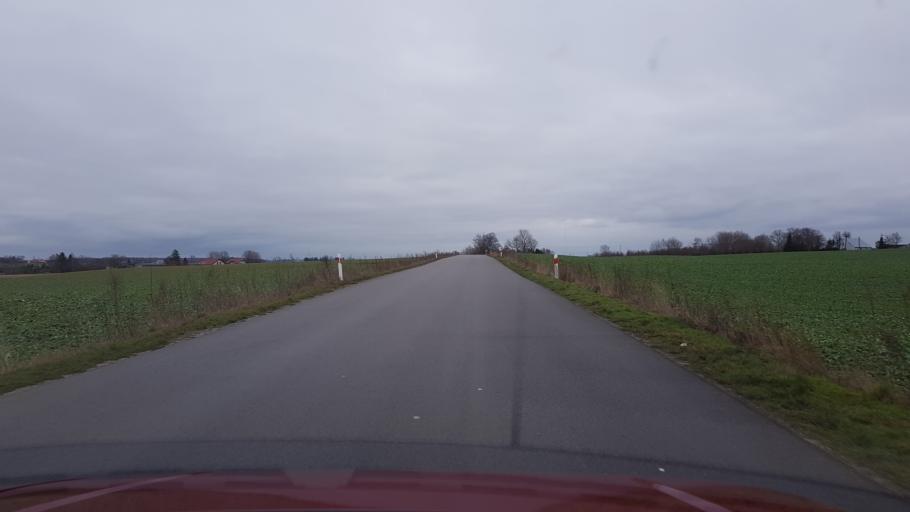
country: PL
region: West Pomeranian Voivodeship
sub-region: Powiat koszalinski
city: Mielno
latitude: 54.1713
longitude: 16.0085
